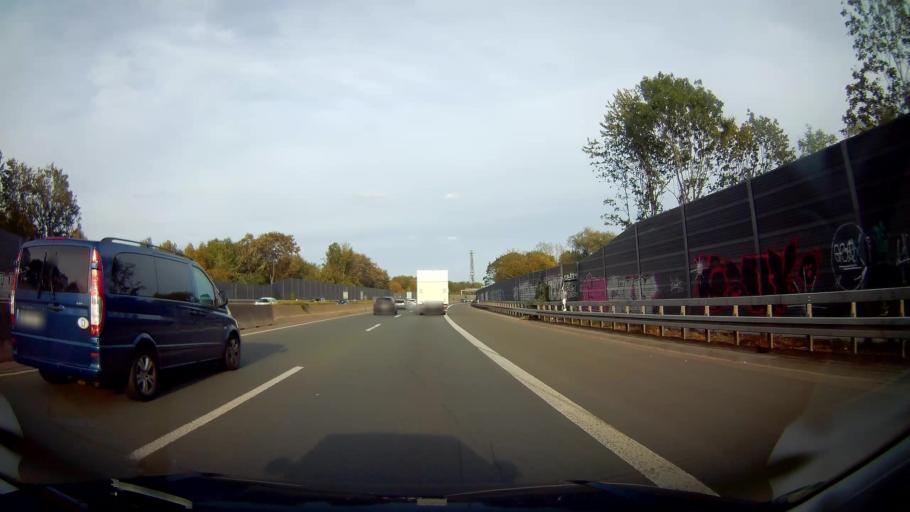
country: DE
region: North Rhine-Westphalia
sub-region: Regierungsbezirk Arnsberg
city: Herne
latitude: 51.5582
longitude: 7.2384
